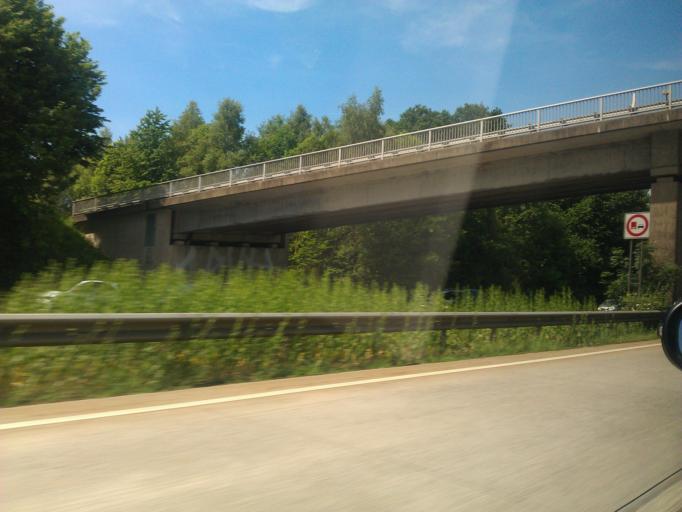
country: DE
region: Rheinland-Pfalz
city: Breitscheid
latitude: 50.6029
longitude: 7.4307
